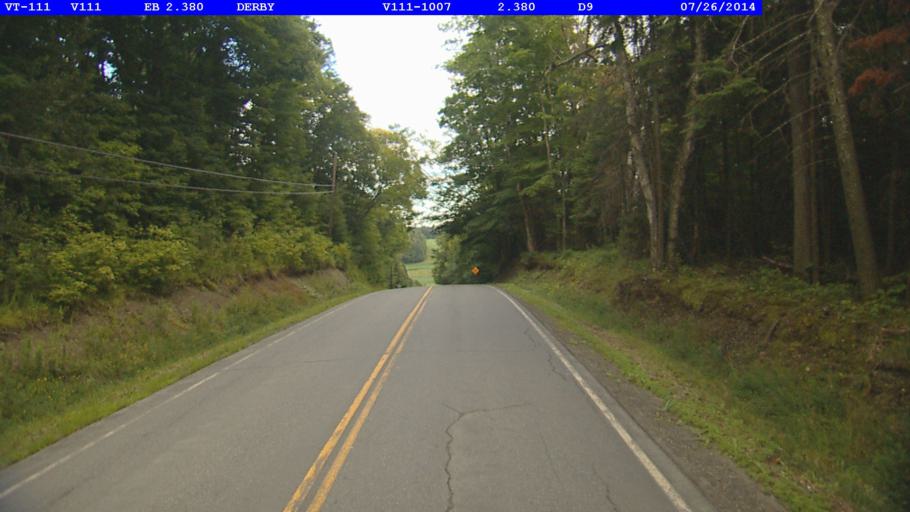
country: US
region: Vermont
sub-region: Orleans County
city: Newport
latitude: 44.9387
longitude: -72.0920
